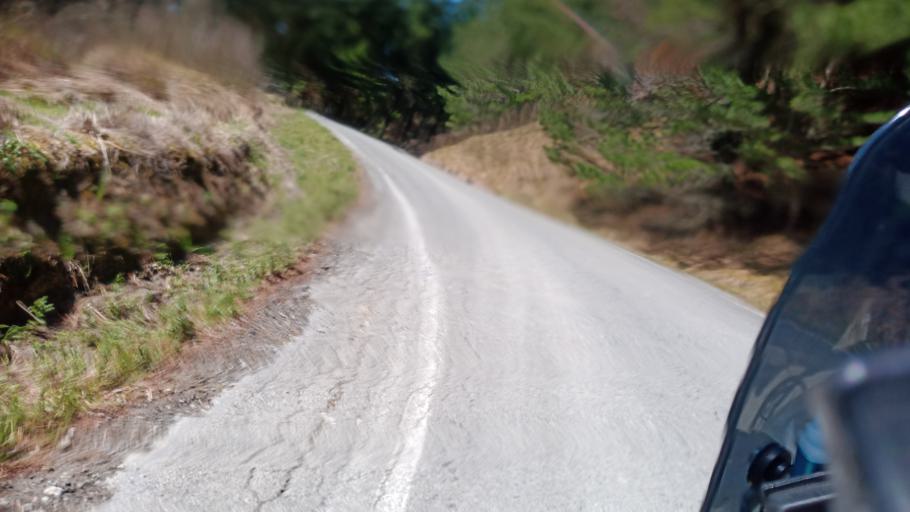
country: NZ
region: Gisborne
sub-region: Gisborne District
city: Gisborne
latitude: -38.7998
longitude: 177.7696
